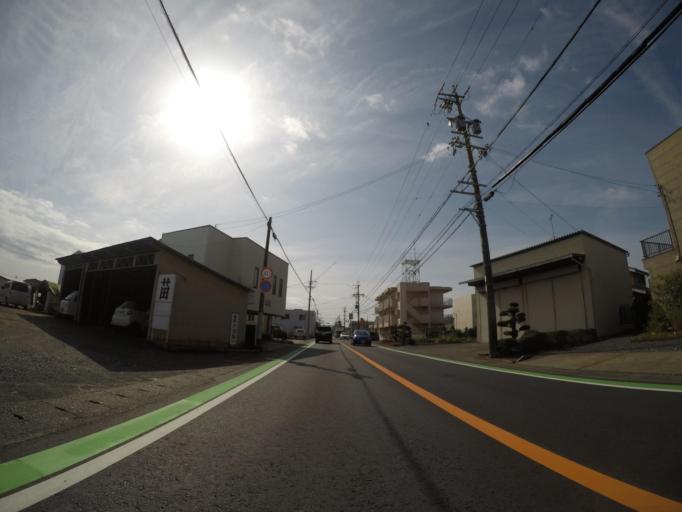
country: JP
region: Shizuoka
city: Hamakita
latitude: 34.7850
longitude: 137.7073
